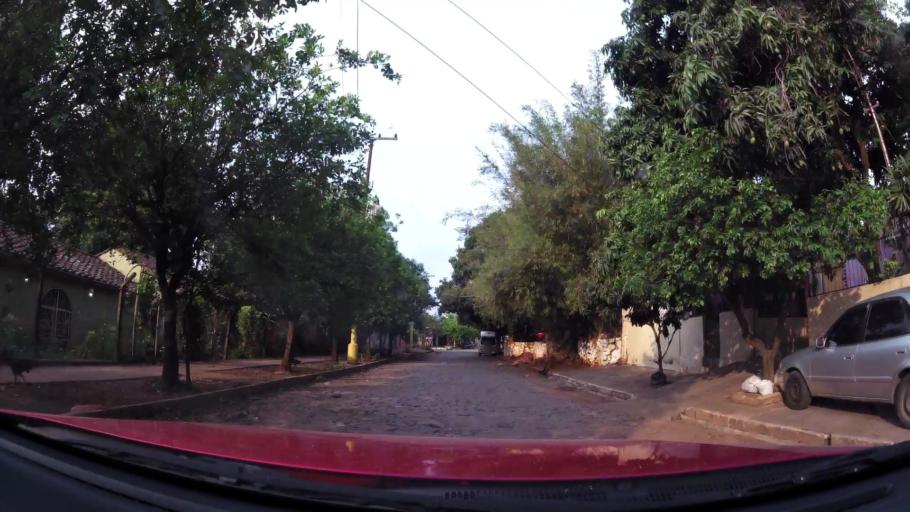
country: PY
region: Central
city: Lambare
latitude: -25.3276
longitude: -57.5781
